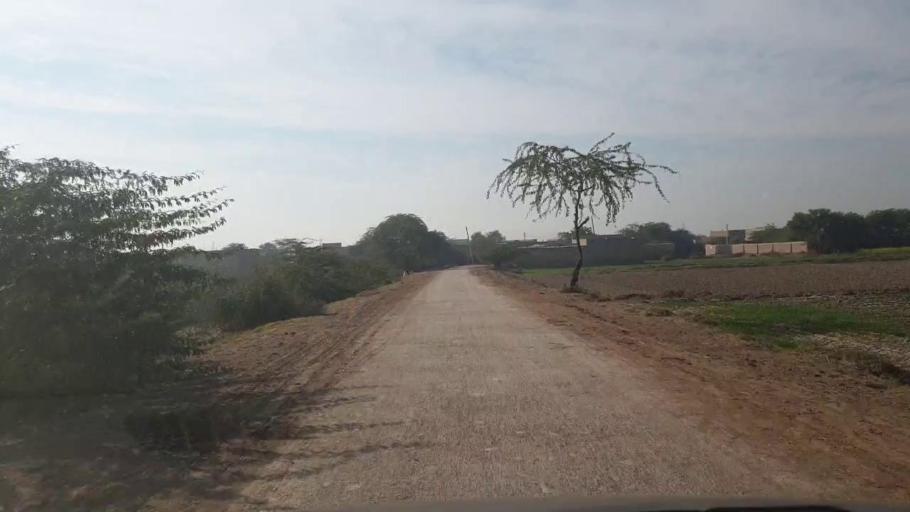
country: PK
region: Sindh
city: Shahpur Chakar
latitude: 26.1752
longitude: 68.5852
